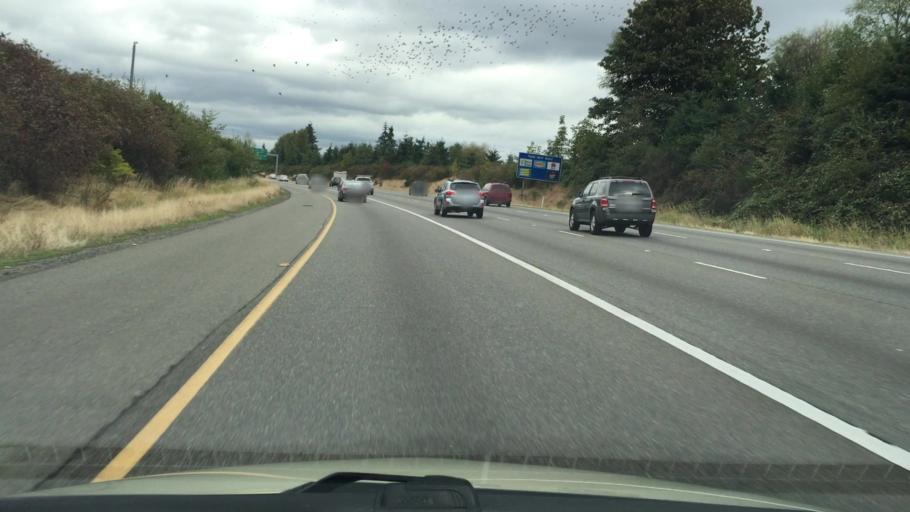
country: US
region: Washington
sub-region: Snohomish County
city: Martha Lake
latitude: 47.8643
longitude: -122.2450
